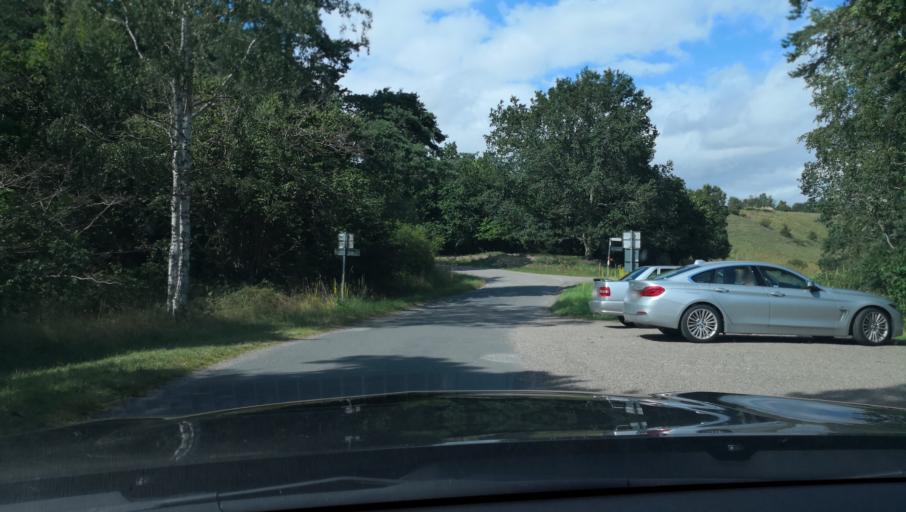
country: SE
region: Skane
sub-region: Ystads Kommun
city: Kopingebro
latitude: 55.3866
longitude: 14.1464
